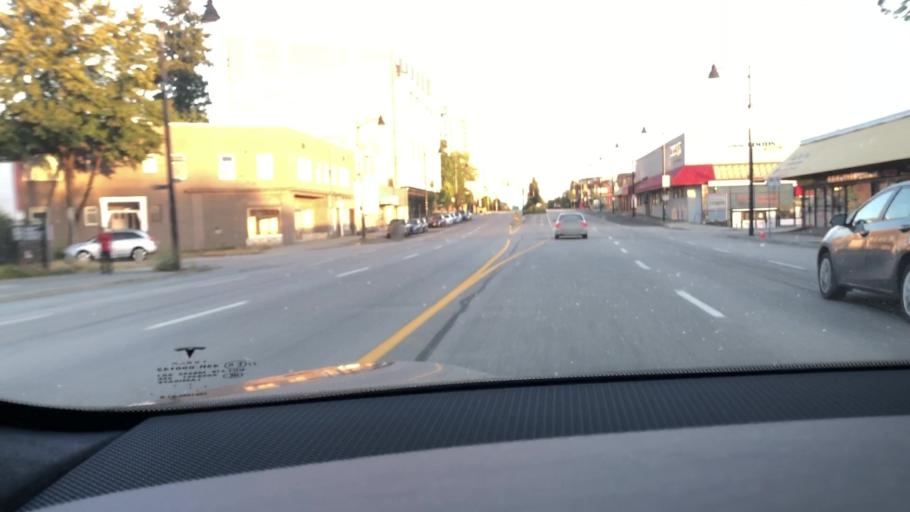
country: CA
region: British Columbia
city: Vancouver
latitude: 49.2478
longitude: -123.0708
